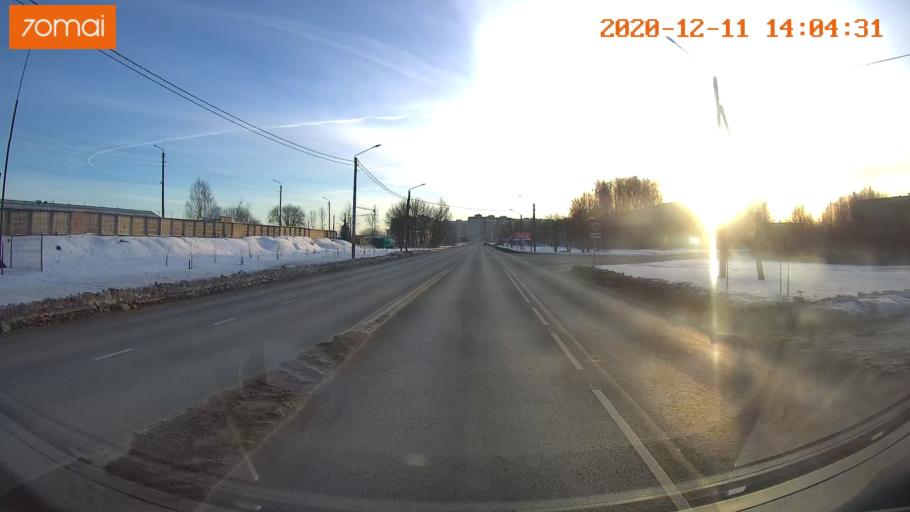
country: RU
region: Kostroma
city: Oktyabr'skiy
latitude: 57.7546
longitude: 41.0164
